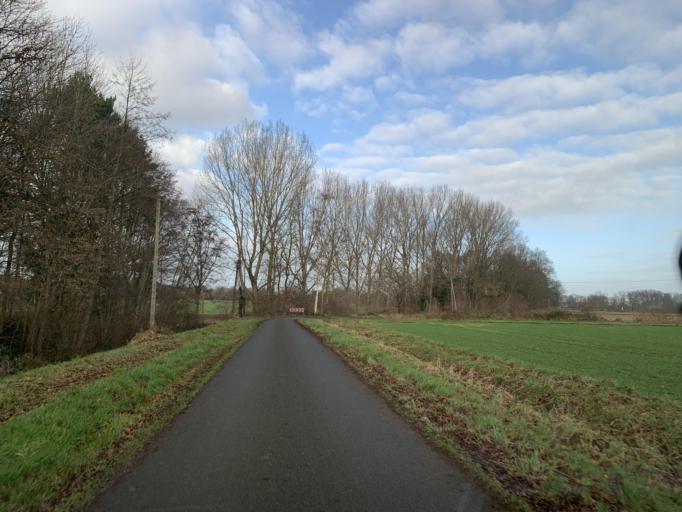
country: DE
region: North Rhine-Westphalia
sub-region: Regierungsbezirk Munster
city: Greven
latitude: 52.0537
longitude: 7.6244
